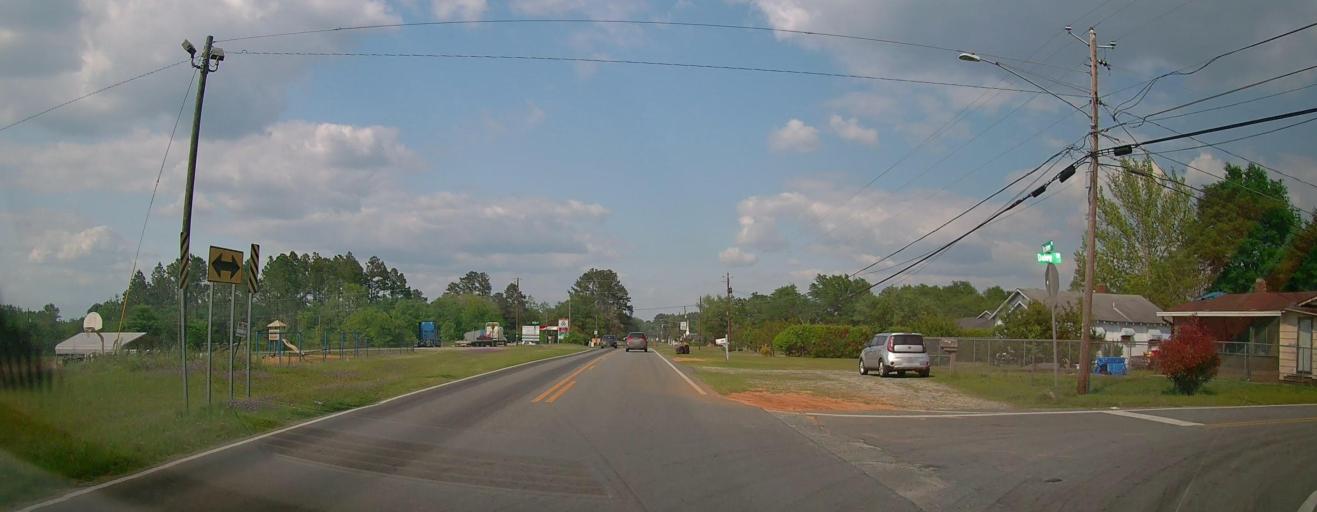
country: US
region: Georgia
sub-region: Laurens County
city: East Dublin
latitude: 32.5548
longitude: -82.8736
